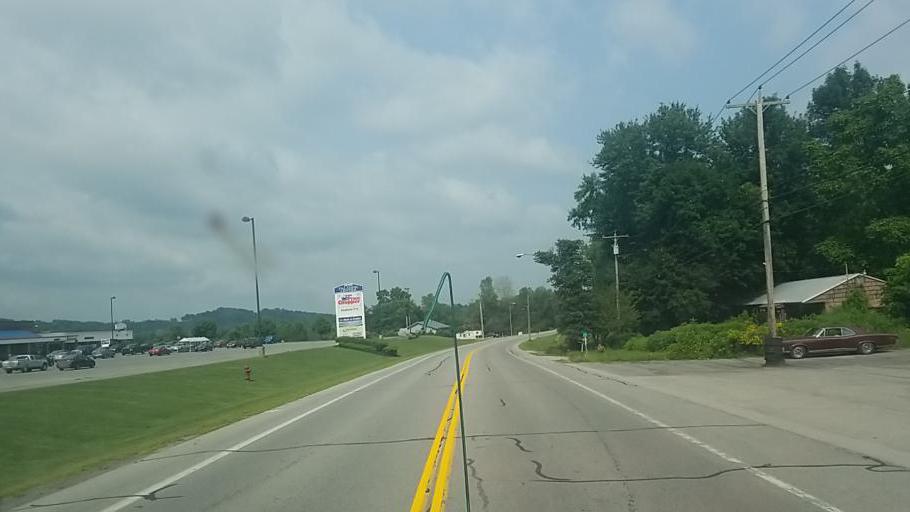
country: US
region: New York
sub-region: Montgomery County
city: Canajoharie
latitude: 42.9155
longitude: -74.5895
